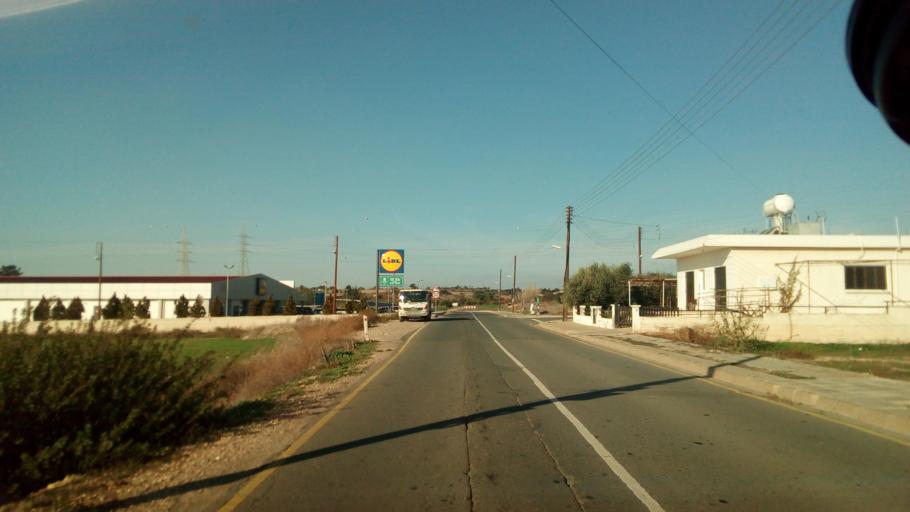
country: CY
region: Larnaka
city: Xylotymbou
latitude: 34.9999
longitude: 33.7599
